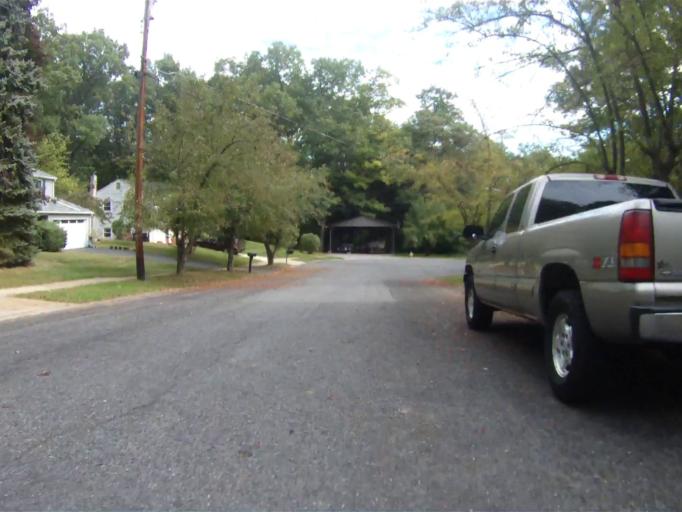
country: US
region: Pennsylvania
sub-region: Centre County
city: Park Forest Village
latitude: 40.8097
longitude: -77.9177
